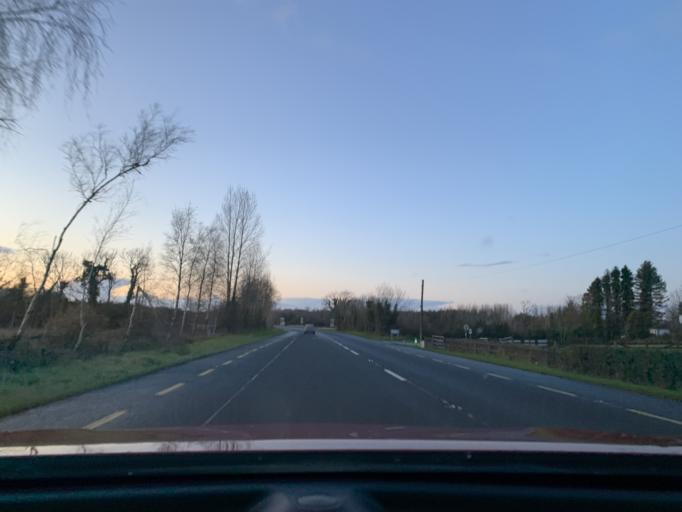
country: IE
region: Connaught
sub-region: County Leitrim
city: Carrick-on-Shannon
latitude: 53.9158
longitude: -7.9747
